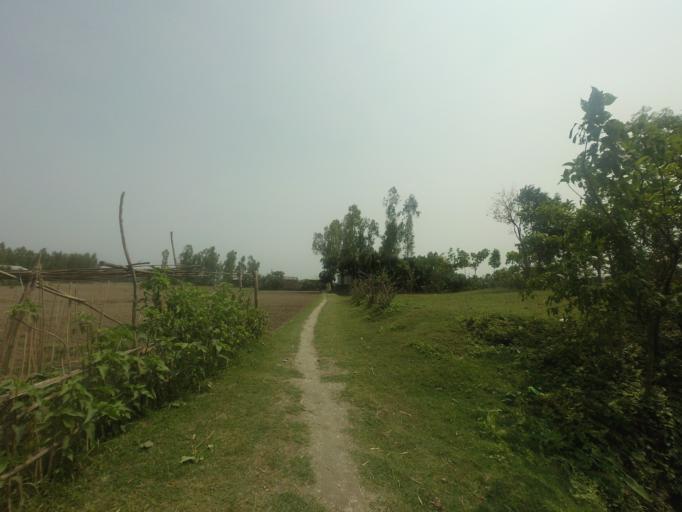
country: BD
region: Rajshahi
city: Sirajganj
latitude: 24.3568
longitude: 89.7217
